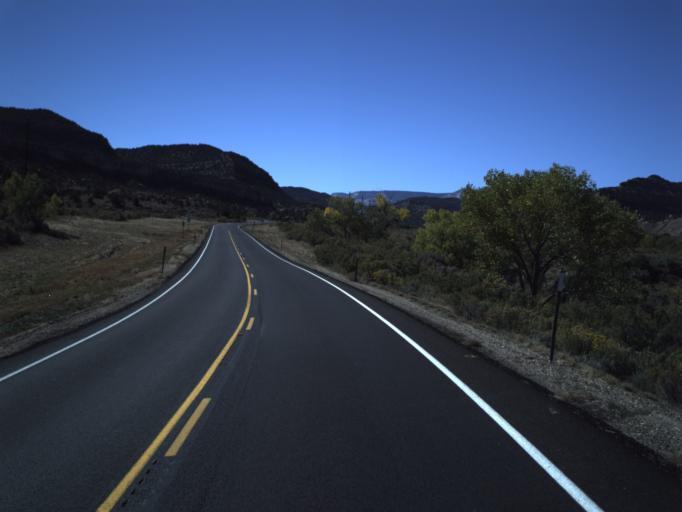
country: US
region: Utah
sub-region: Wayne County
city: Loa
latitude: 37.7721
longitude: -111.6589
